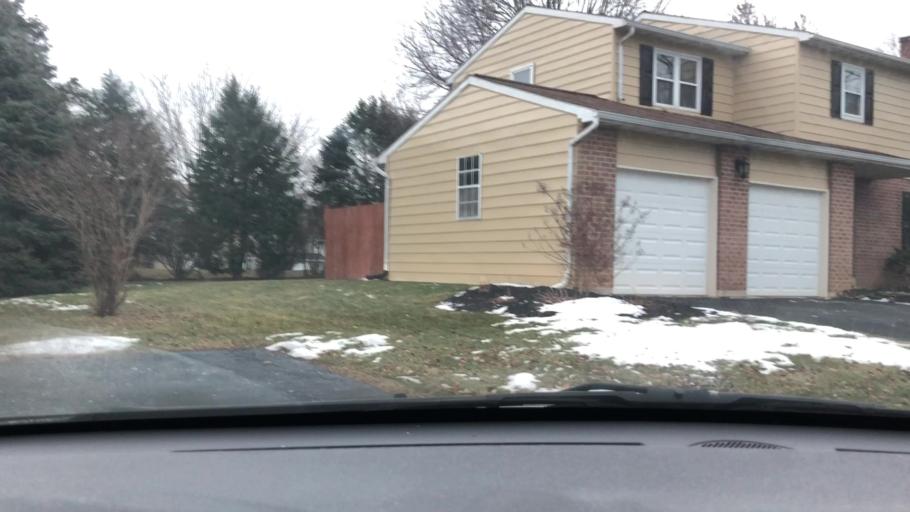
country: US
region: Pennsylvania
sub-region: Lancaster County
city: Mountville
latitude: 40.0678
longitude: -76.4656
